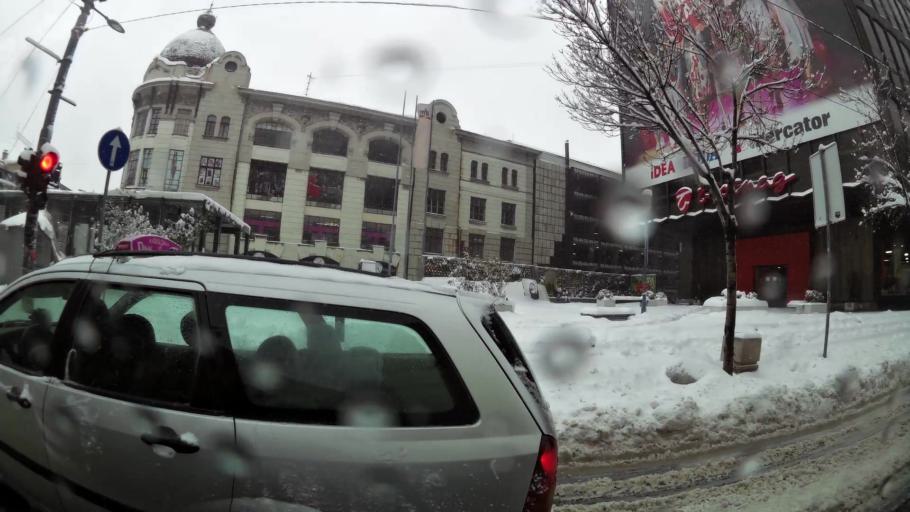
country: RS
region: Central Serbia
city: Belgrade
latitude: 44.8069
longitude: 20.4643
